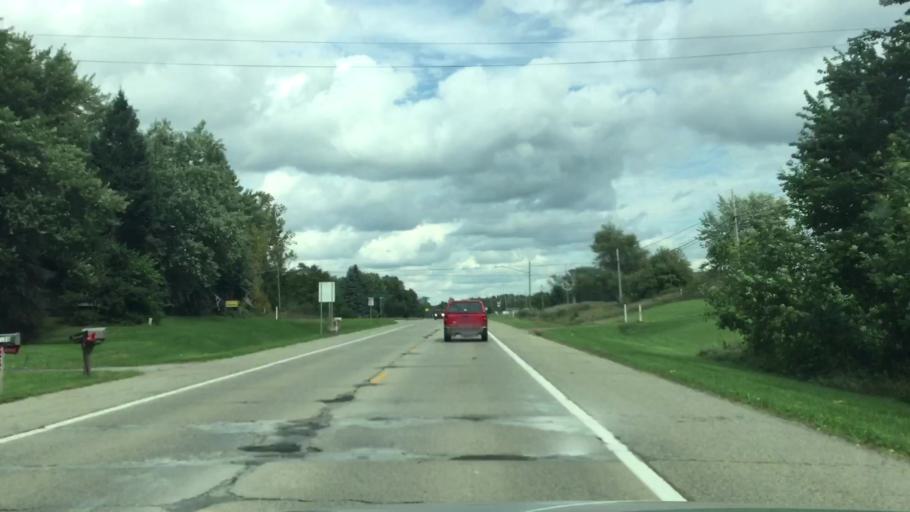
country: US
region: Michigan
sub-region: Shiawassee County
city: Owosso
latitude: 42.9667
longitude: -84.1953
